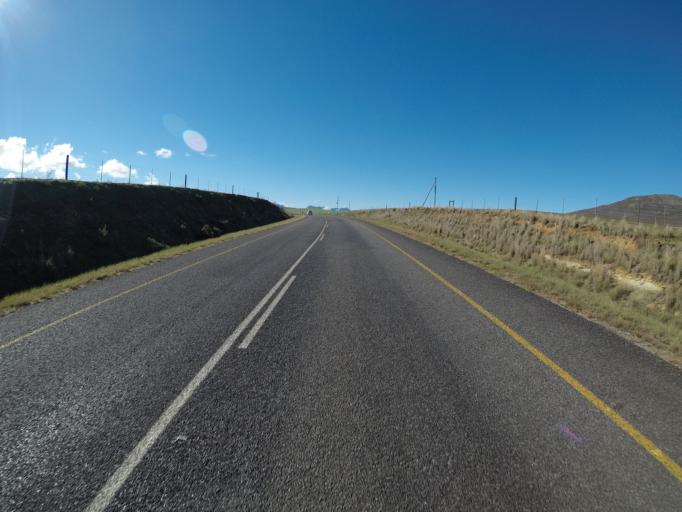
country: ZA
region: Western Cape
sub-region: Overberg District Municipality
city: Caledon
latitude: -34.1549
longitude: 19.4699
